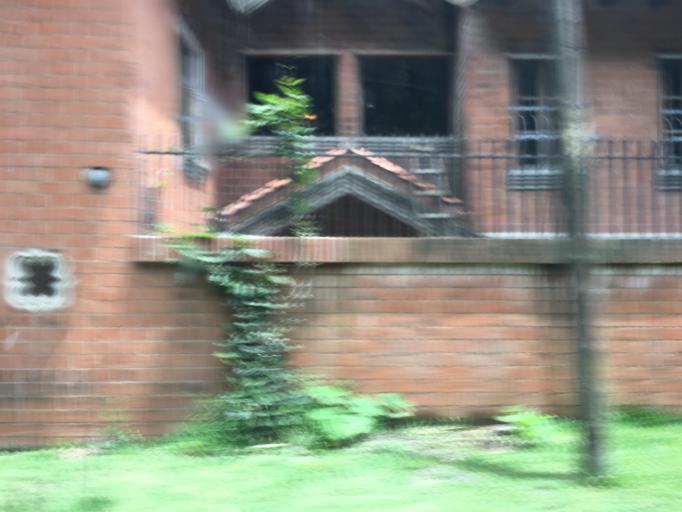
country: GT
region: Guatemala
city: Villa Canales
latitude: 14.4203
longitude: -90.5383
